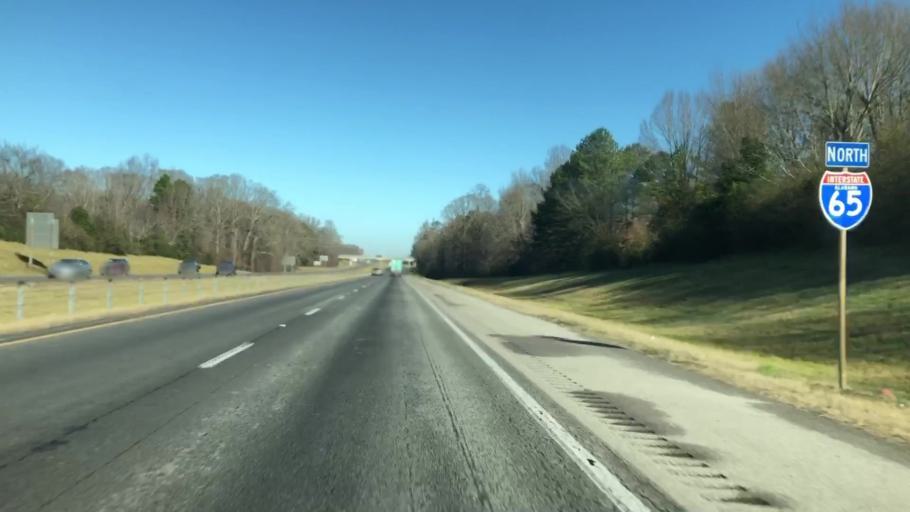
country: US
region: Alabama
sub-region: Limestone County
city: Athens
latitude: 34.7906
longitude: -86.9393
